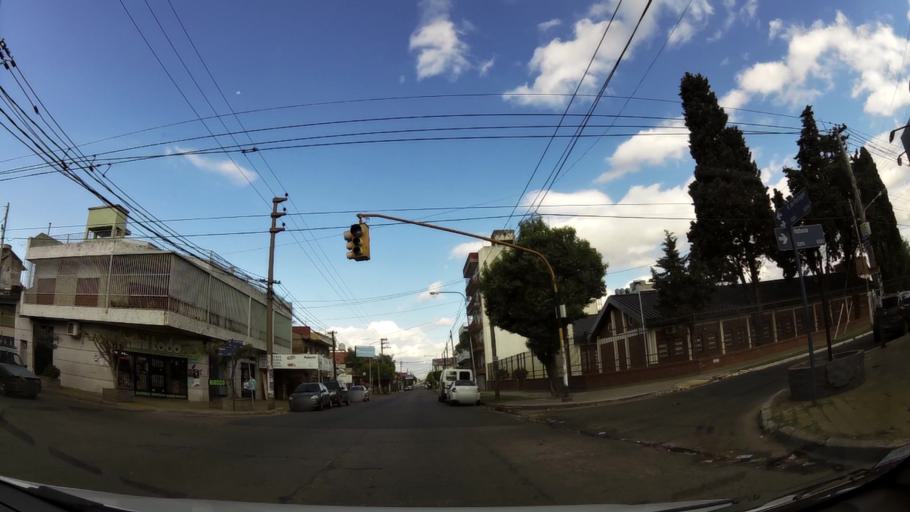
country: AR
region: Buenos Aires
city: San Justo
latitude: -34.6996
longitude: -58.5942
